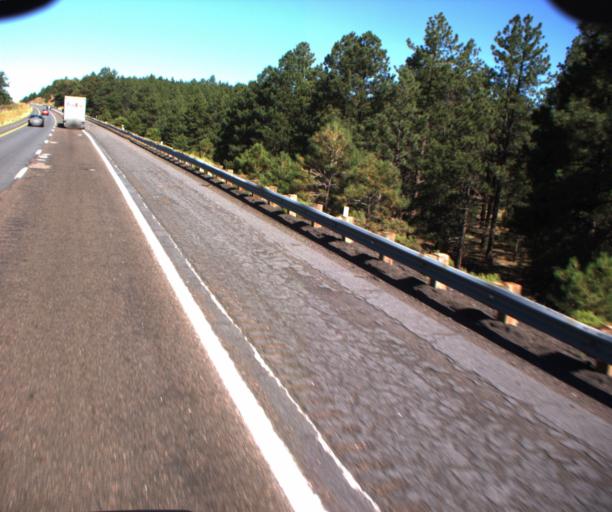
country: US
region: Arizona
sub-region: Coconino County
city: Parks
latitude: 35.2522
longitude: -111.9977
